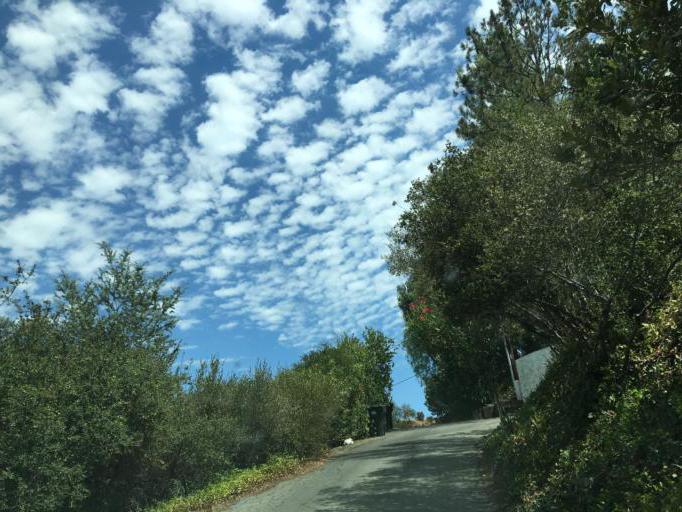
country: US
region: California
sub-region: Los Angeles County
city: Agoura Hills
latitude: 34.1060
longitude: -118.7565
